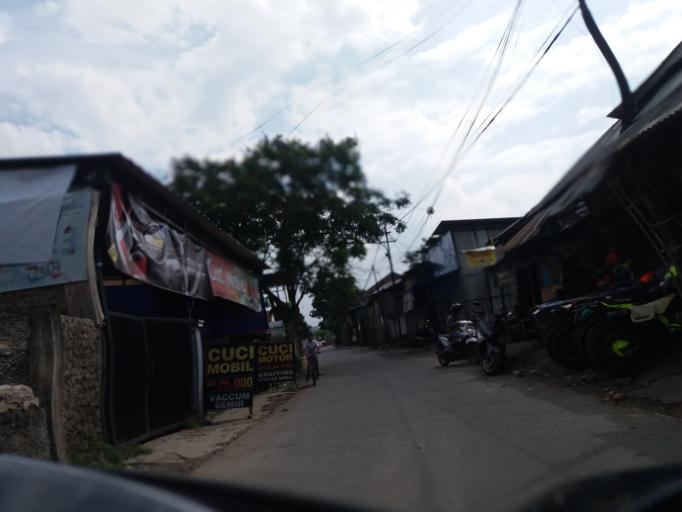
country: ID
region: West Java
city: Bandung
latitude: -6.9255
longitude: 107.6562
